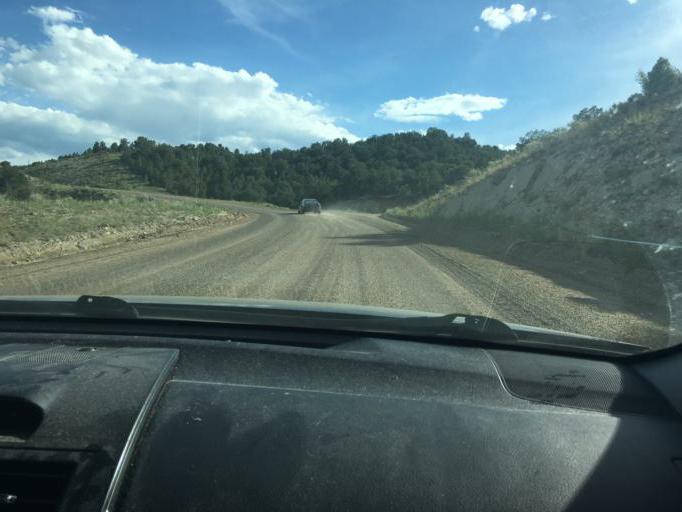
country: US
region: Colorado
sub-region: Eagle County
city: Edwards
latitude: 39.8678
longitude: -106.6435
